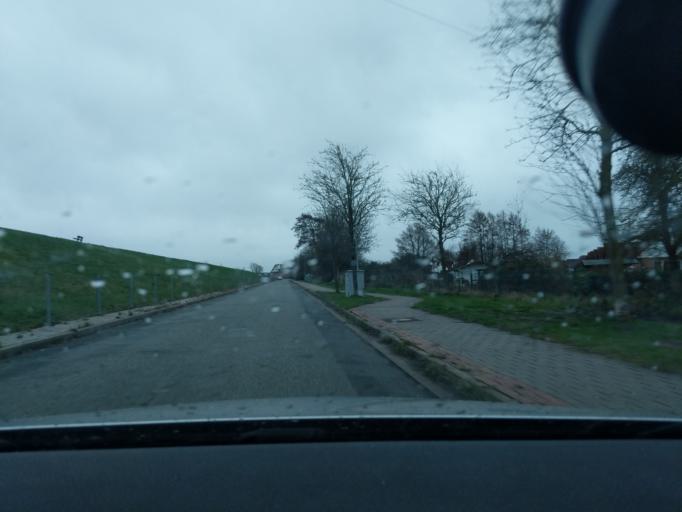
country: DE
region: Schleswig-Holstein
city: Haseldorf
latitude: 53.5974
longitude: 9.5669
